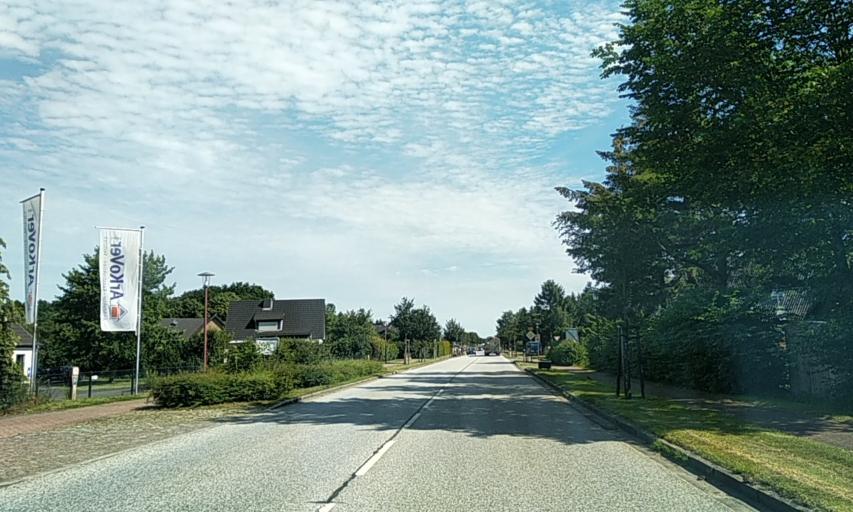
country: DE
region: Schleswig-Holstein
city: Jagel
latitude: 54.4575
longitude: 9.5377
